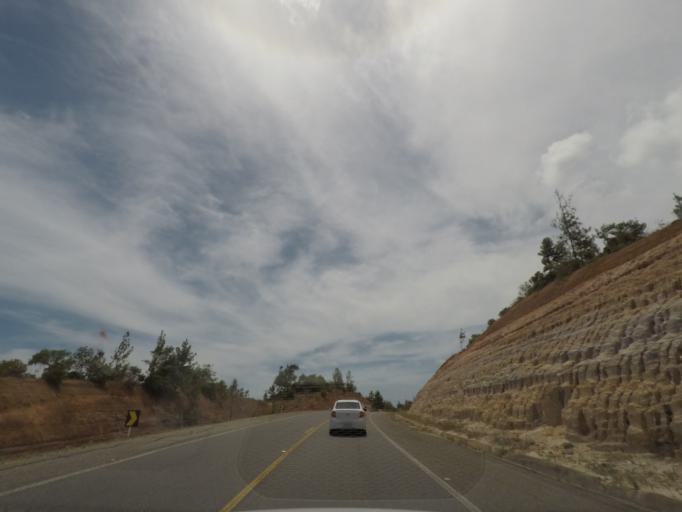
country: BR
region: Bahia
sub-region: Conde
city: Conde
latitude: -11.9933
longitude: -37.6788
